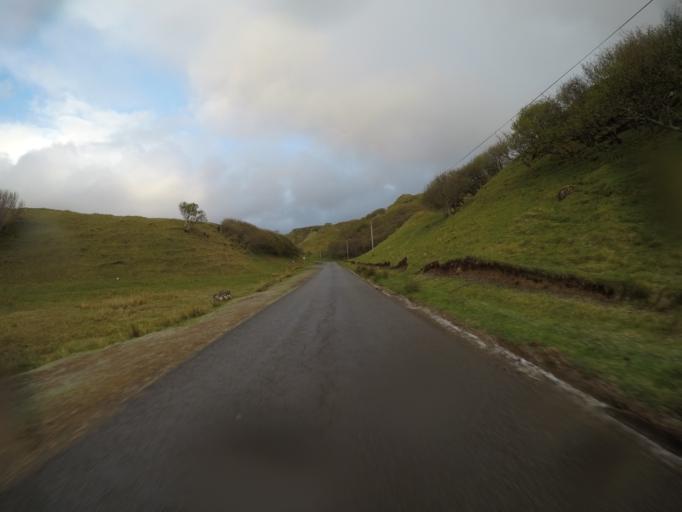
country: GB
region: Scotland
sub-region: Highland
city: Portree
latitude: 57.5842
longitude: -6.3322
